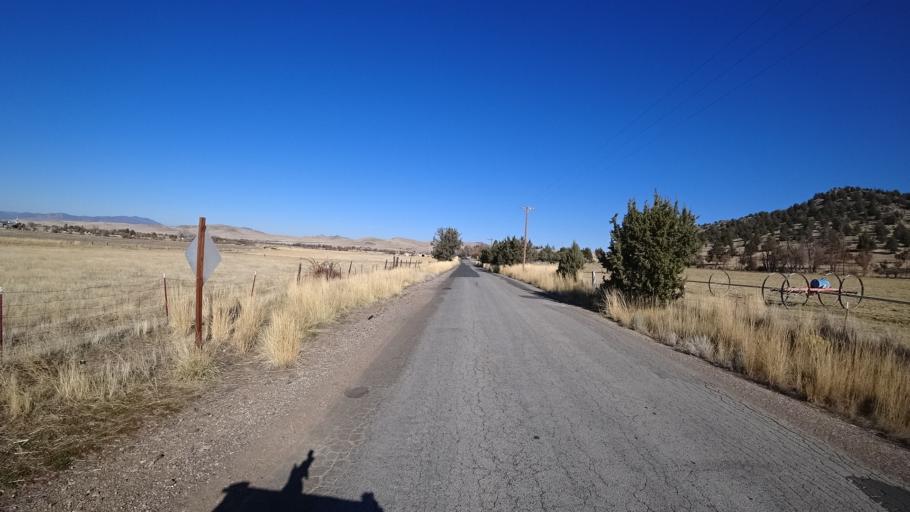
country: US
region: California
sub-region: Siskiyou County
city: Montague
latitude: 41.7067
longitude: -122.3793
